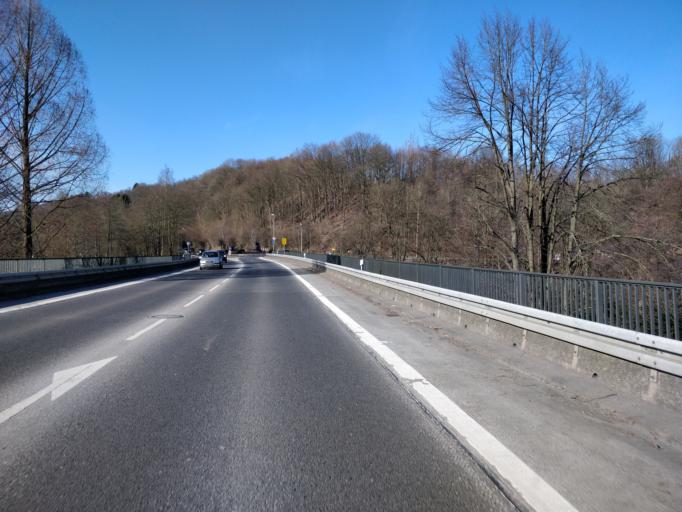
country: DE
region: North Rhine-Westphalia
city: Wiehl
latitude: 50.9479
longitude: 7.5440
